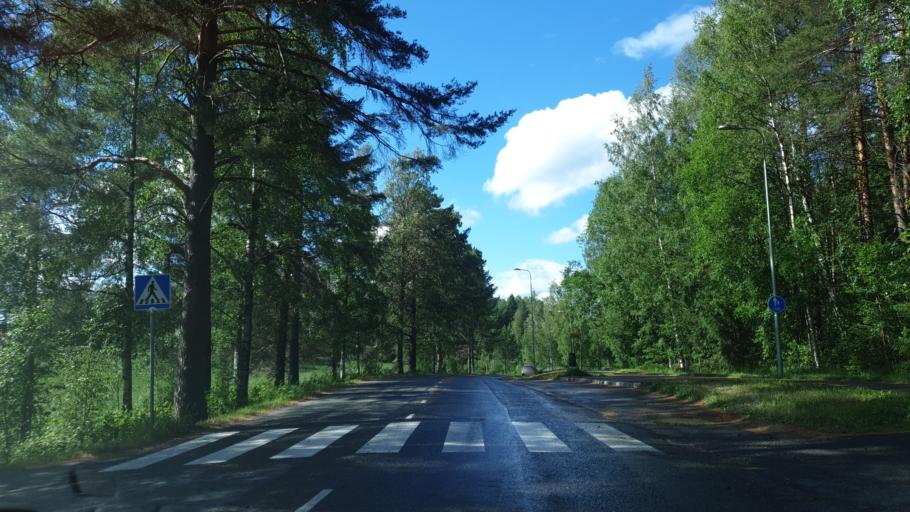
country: FI
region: Northern Savo
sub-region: Kuopio
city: Kuopio
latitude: 62.9175
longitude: 27.6309
